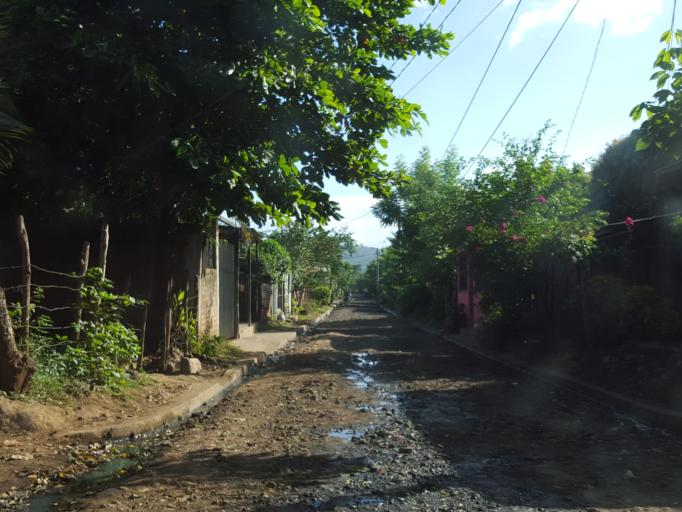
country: NI
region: Leon
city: Leon
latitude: 12.4236
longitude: -86.9080
